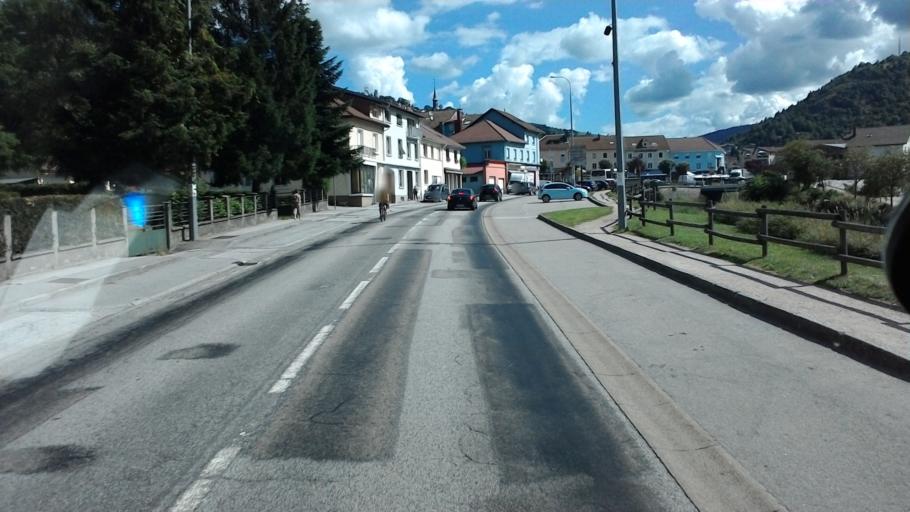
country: FR
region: Lorraine
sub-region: Departement des Vosges
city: La Bresse
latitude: 48.0024
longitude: 6.8725
